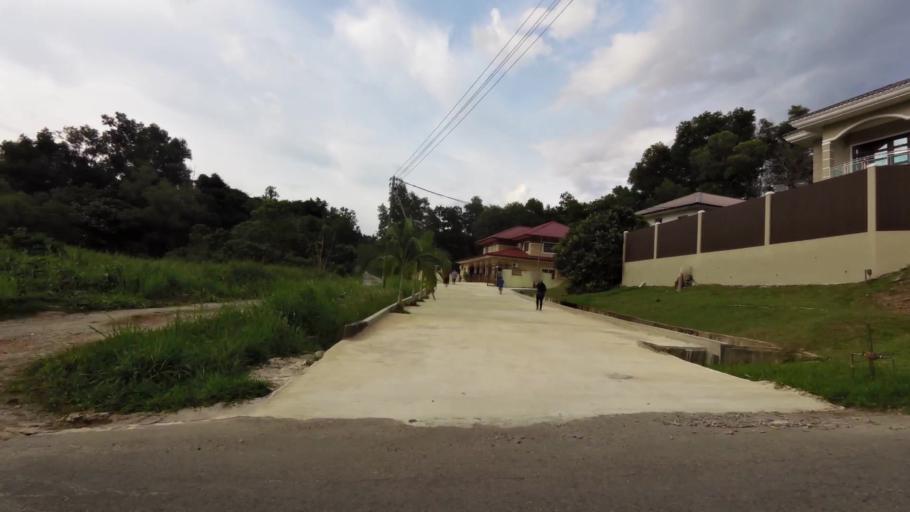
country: BN
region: Brunei and Muara
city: Bandar Seri Begawan
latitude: 4.9523
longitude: 114.9764
